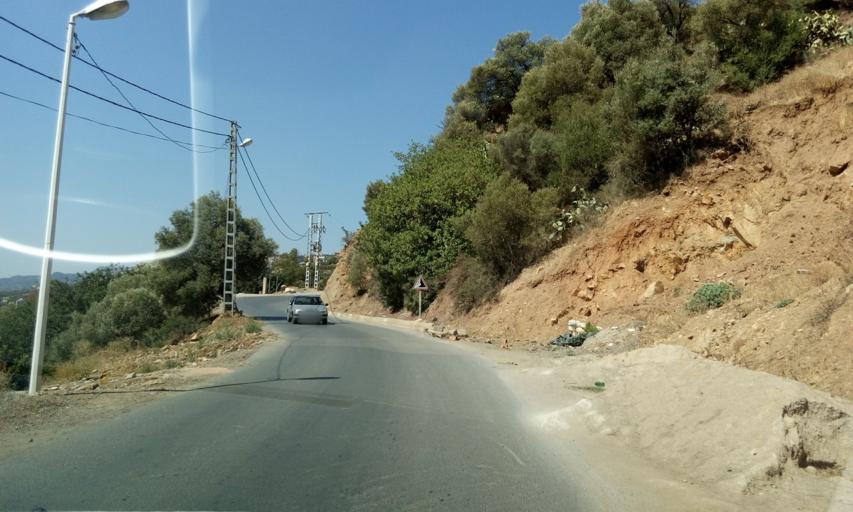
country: DZ
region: Tizi Ouzou
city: Chemini
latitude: 36.6068
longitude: 4.6448
